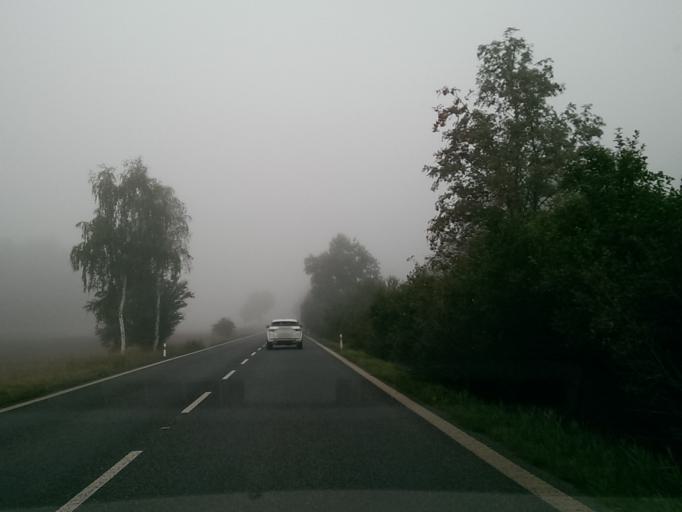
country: CZ
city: Doksy
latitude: 50.5985
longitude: 14.6015
